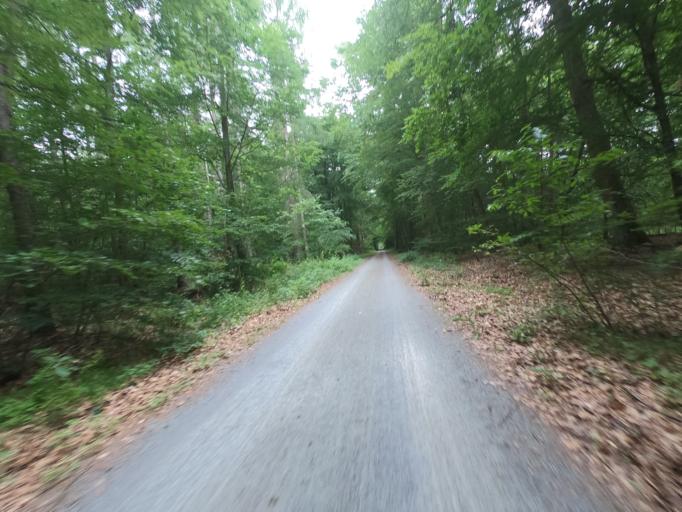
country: DE
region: Hesse
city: Langen
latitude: 50.0264
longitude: 8.6283
